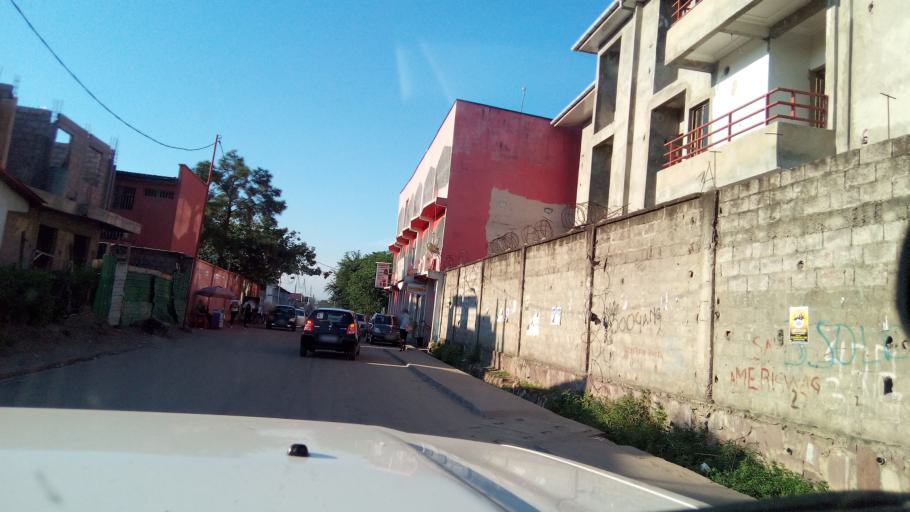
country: CD
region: Kinshasa
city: Kinshasa
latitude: -4.3402
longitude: 15.2672
